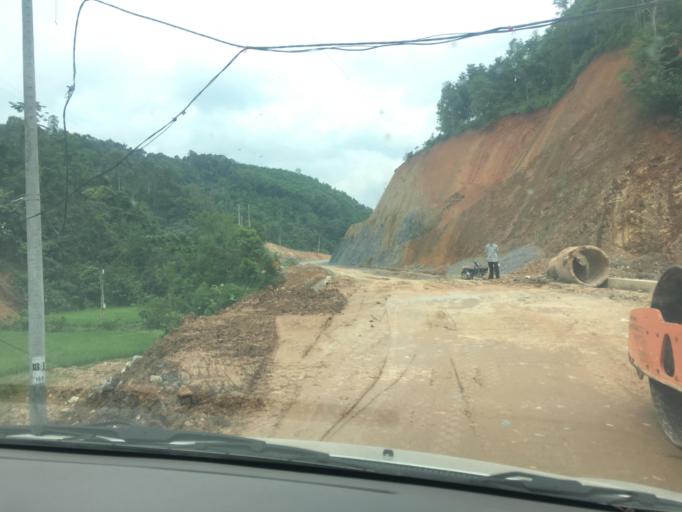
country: VN
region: Bac Kan
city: Yen Lac
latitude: 22.1662
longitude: 106.3017
